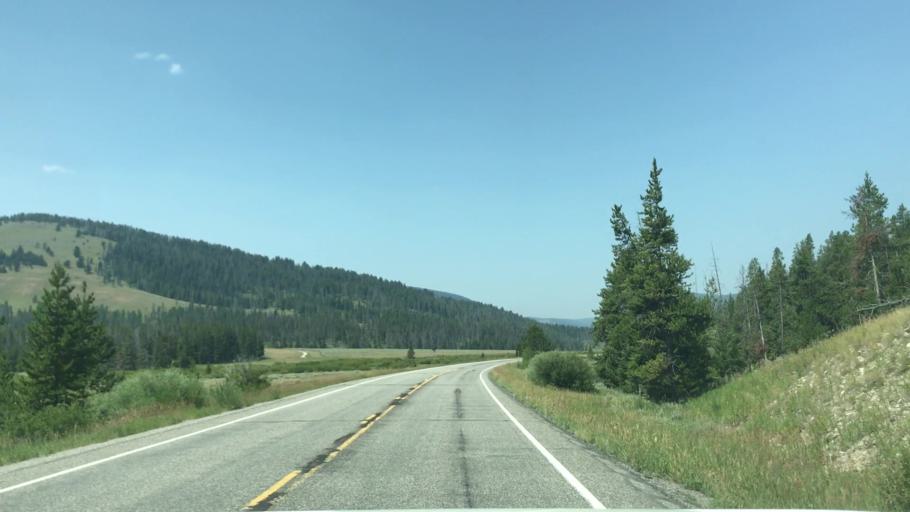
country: US
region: Montana
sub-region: Gallatin County
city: West Yellowstone
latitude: 45.0270
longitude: -111.1045
